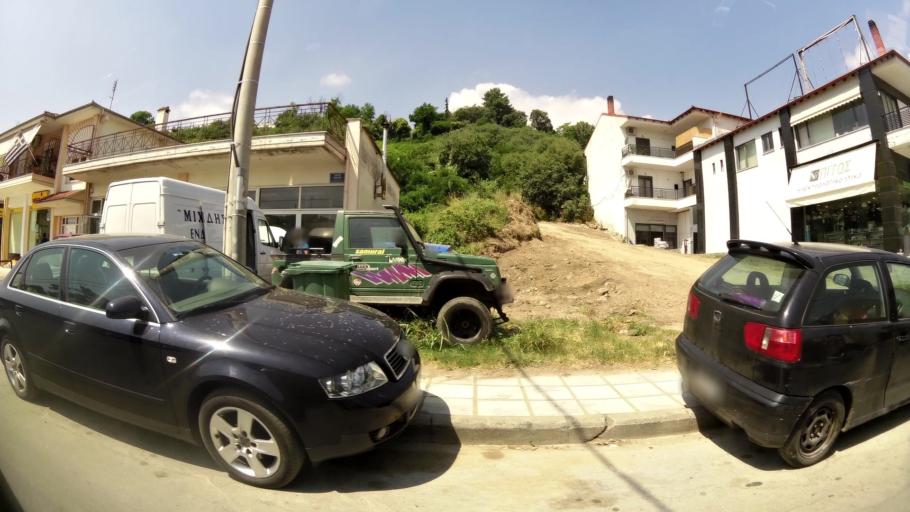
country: GR
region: Central Macedonia
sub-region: Nomos Imathias
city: Veroia
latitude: 40.5292
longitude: 22.2083
